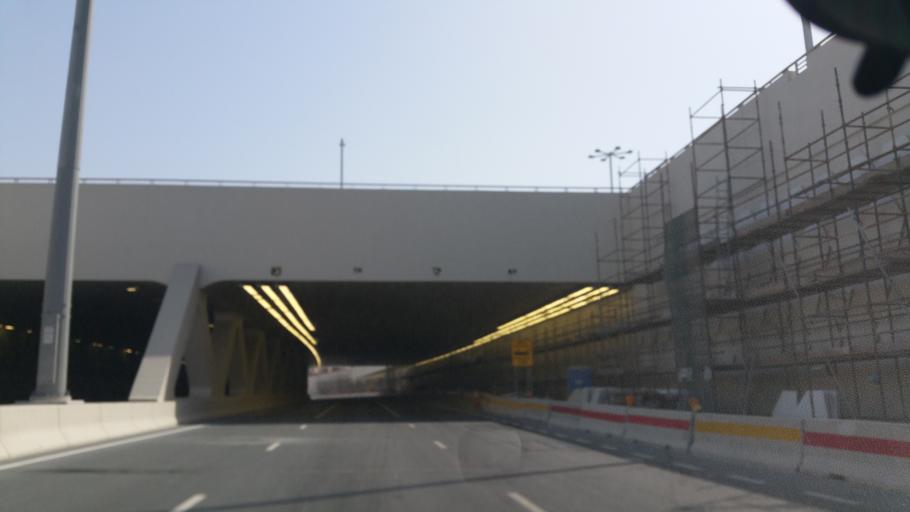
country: QA
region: Baladiyat Umm Salal
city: Umm Salal Muhammad
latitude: 25.4267
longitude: 51.5089
